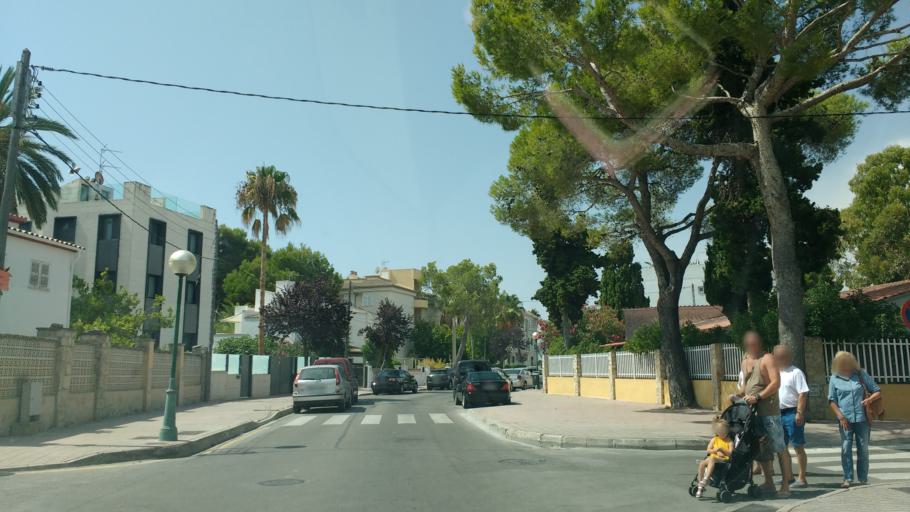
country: ES
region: Balearic Islands
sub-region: Illes Balears
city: Port d'Alcudia
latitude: 39.8398
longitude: 3.1255
